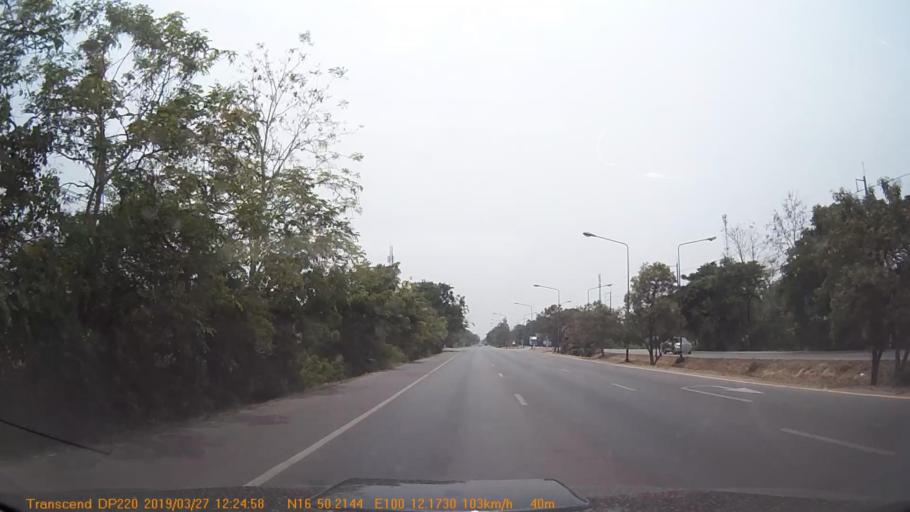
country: TH
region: Phitsanulok
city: Phitsanulok
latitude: 16.8367
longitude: 100.2029
